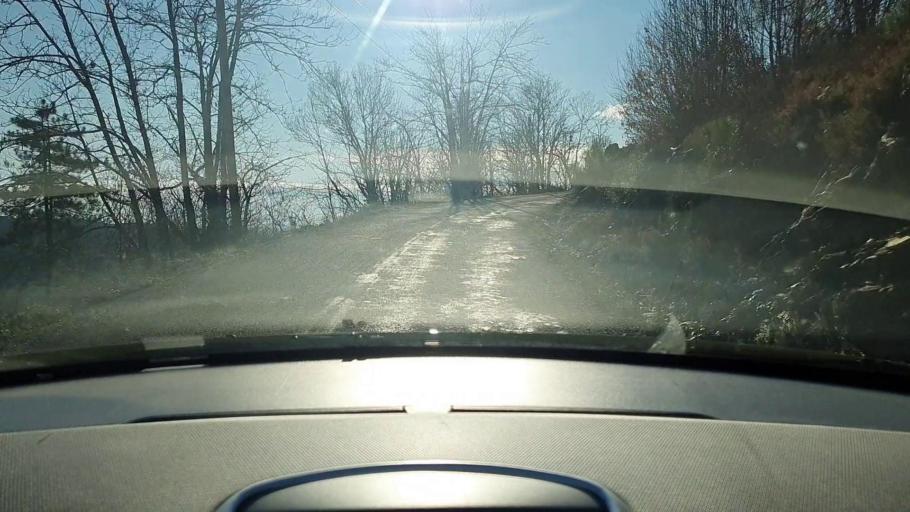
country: FR
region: Languedoc-Roussillon
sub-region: Departement du Gard
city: Branoux-les-Taillades
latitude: 44.2796
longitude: 3.9604
